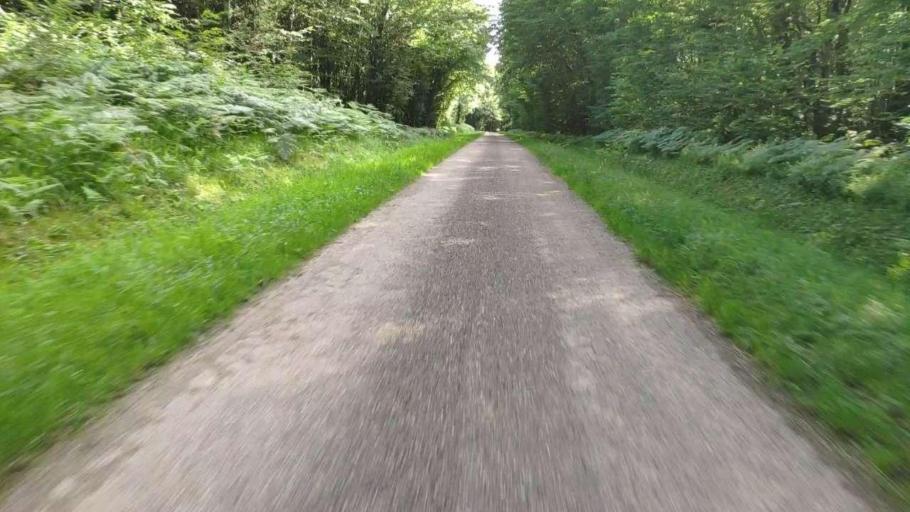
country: FR
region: Franche-Comte
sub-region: Departement du Jura
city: Bletterans
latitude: 46.8171
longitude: 5.5190
